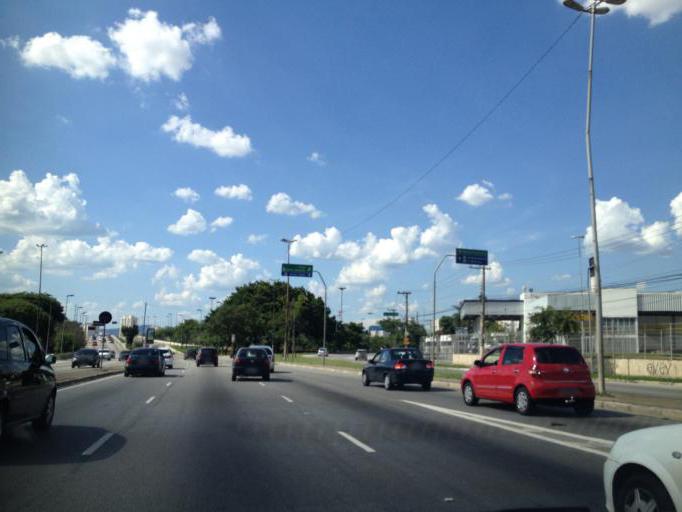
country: BR
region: Sao Paulo
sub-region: Sao Paulo
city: Sao Paulo
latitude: -23.5316
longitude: -46.5837
